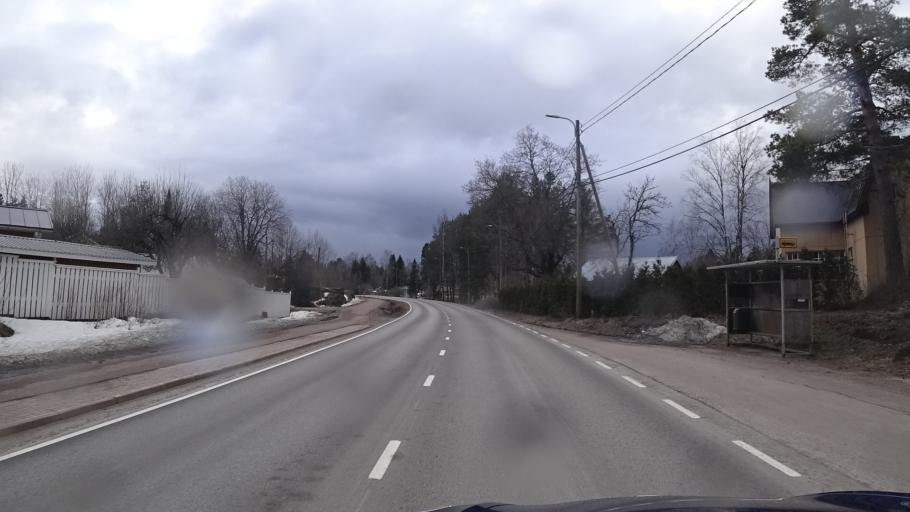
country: FI
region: Kymenlaakso
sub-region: Kotka-Hamina
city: Karhula
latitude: 60.5296
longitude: 26.9041
